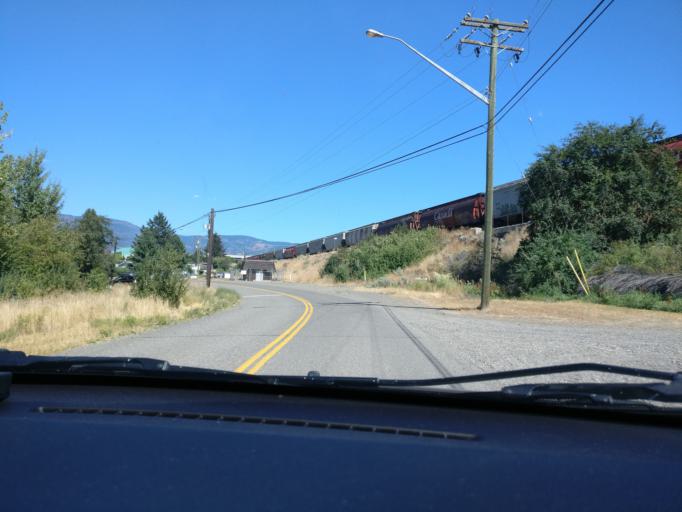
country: CA
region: British Columbia
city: Logan Lake
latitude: 50.7590
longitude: -120.8179
